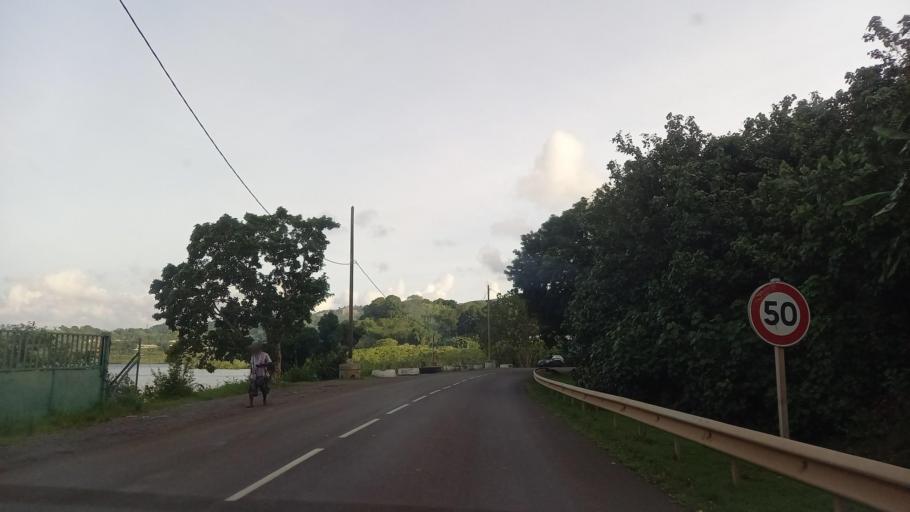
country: YT
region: Koungou
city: Koungou
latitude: -12.7234
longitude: 45.1696
